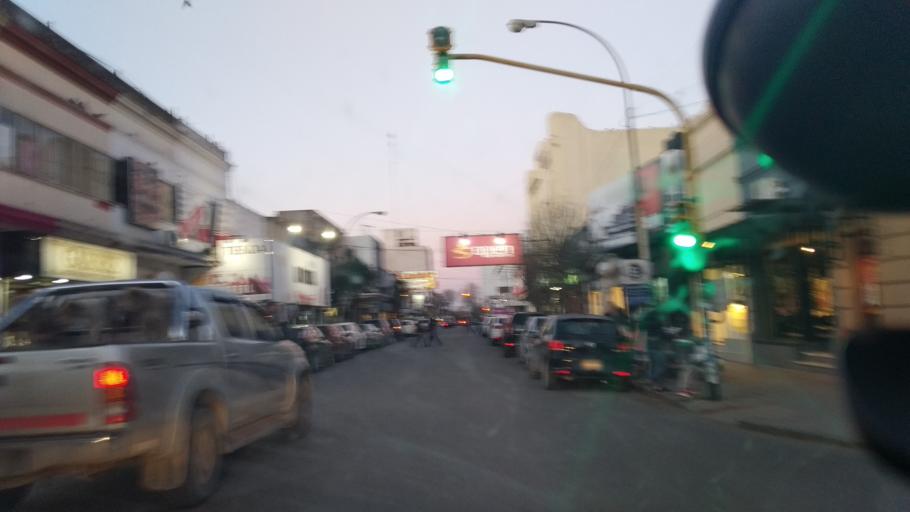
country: AR
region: Buenos Aires
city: Necochea
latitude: -38.5538
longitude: -58.7424
